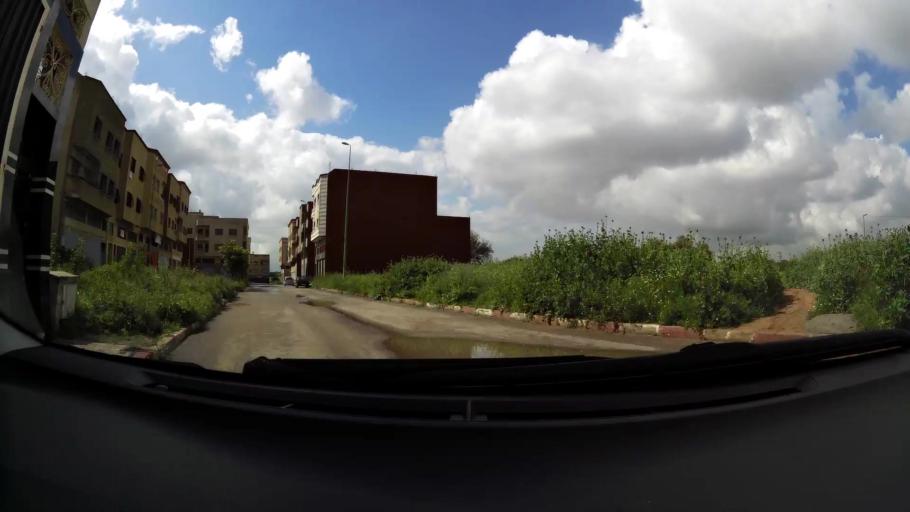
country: MA
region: Grand Casablanca
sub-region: Mediouna
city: Tit Mellil
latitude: 33.5478
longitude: -7.4910
